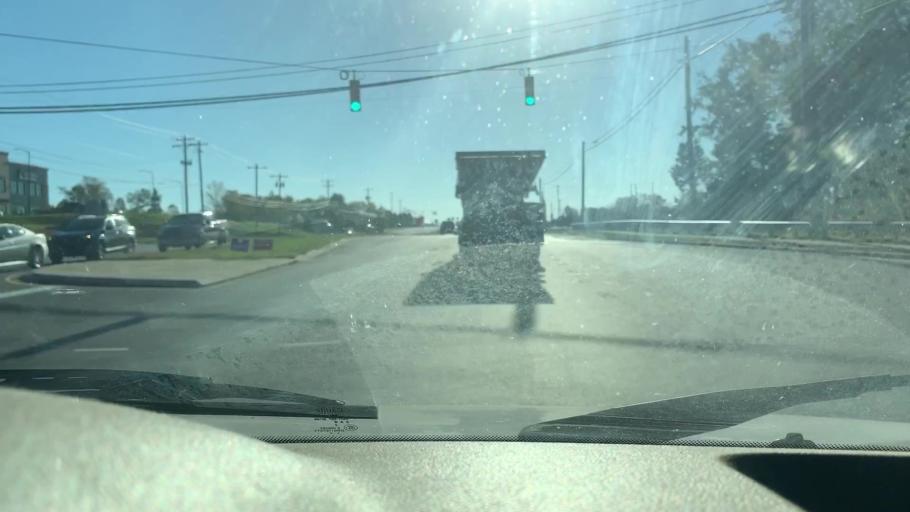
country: US
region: North Carolina
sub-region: Cabarrus County
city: Harrisburg
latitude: 35.4087
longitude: -80.7167
